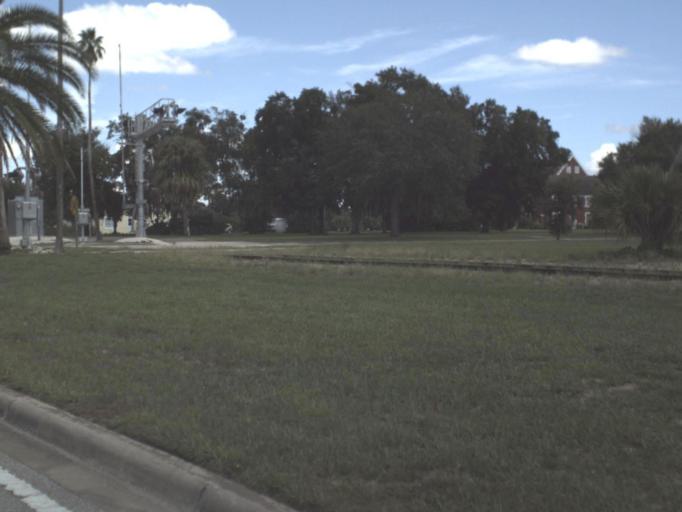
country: US
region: Florida
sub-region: Polk County
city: Lake Wales
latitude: 27.9008
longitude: -81.5861
